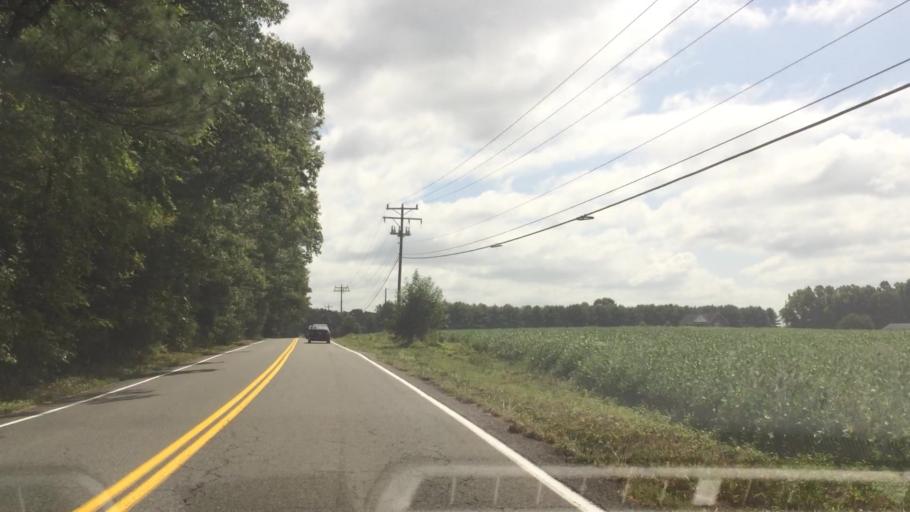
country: US
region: Virginia
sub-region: Henrico County
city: Chamberlayne
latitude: 37.6871
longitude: -77.4363
